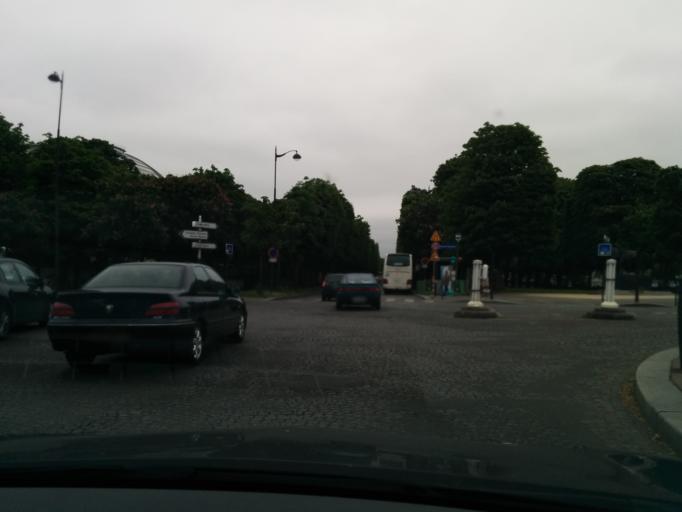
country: FR
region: Ile-de-France
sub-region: Departement des Hauts-de-Seine
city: Clichy
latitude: 48.8646
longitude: 2.3099
